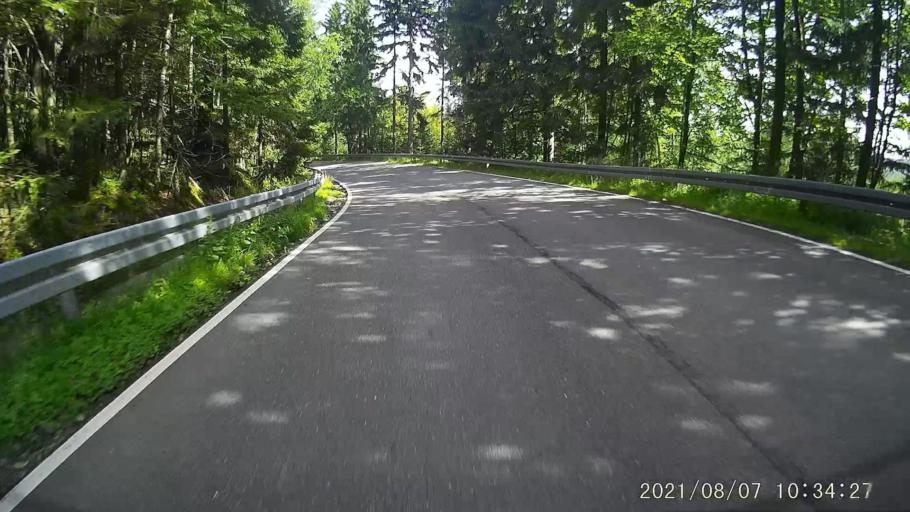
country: PL
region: Lower Silesian Voivodeship
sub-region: Powiat klodzki
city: Duszniki-Zdroj
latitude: 50.3739
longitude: 16.3657
